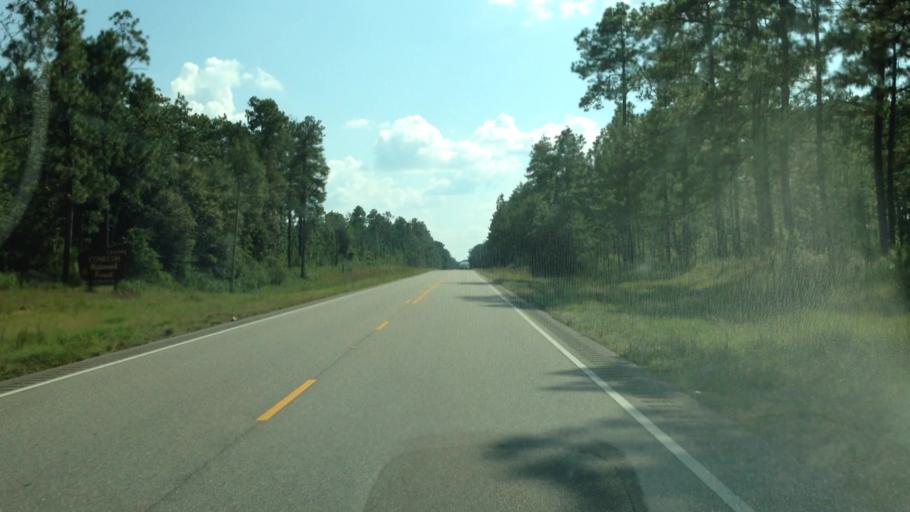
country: US
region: Florida
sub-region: Okaloosa County
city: Crestview
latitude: 31.0027
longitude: -86.6252
